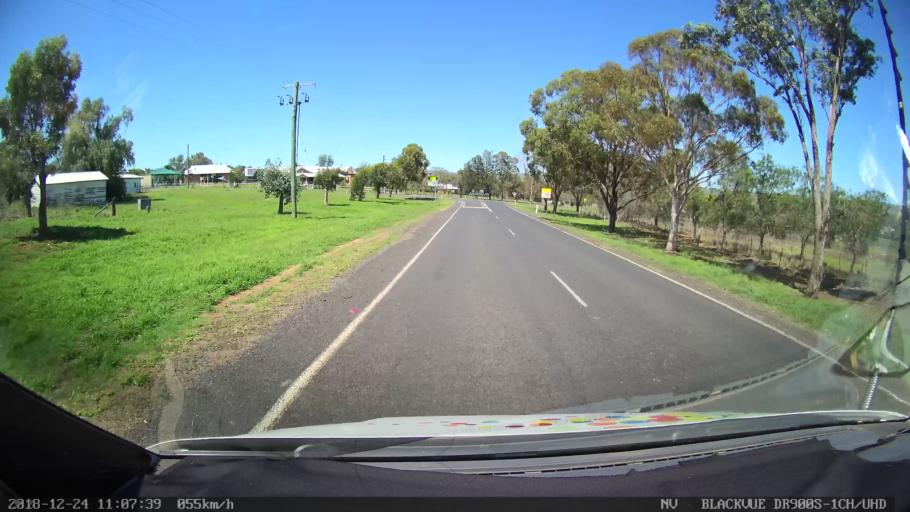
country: AU
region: New South Wales
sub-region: Upper Hunter Shire
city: Merriwa
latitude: -32.1345
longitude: 150.3585
